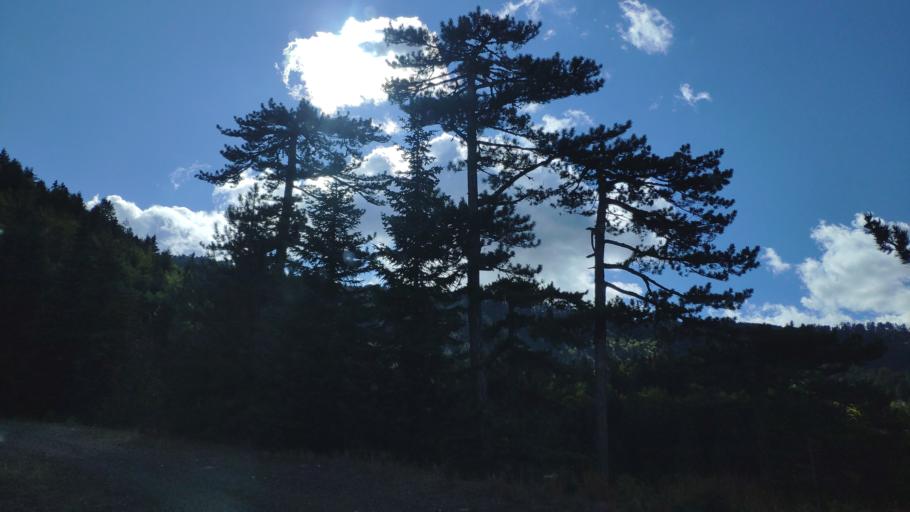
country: GR
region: Epirus
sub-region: Nomos Ioanninon
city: Metsovo
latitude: 39.8916
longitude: 21.2165
